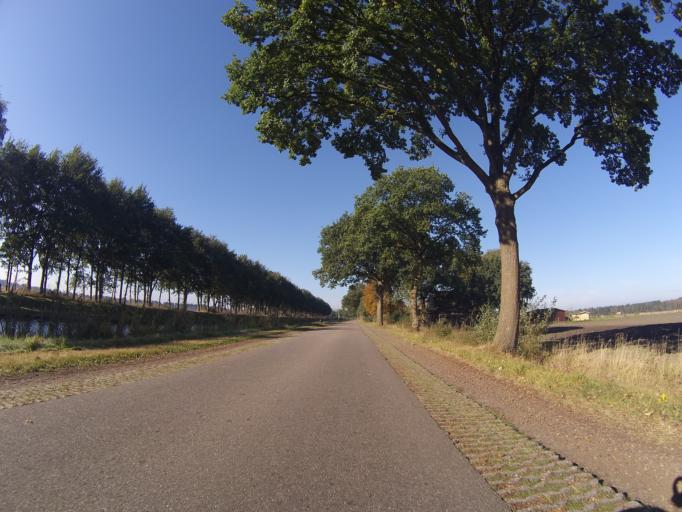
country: NL
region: Drenthe
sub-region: Gemeente Coevorden
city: Dalen
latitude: 52.7424
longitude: 6.7632
